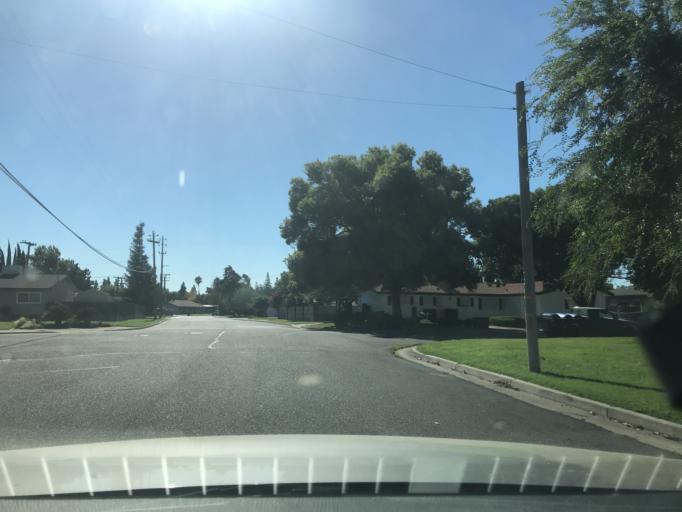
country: US
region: California
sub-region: Merced County
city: Atwater
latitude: 37.3484
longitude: -120.5920
